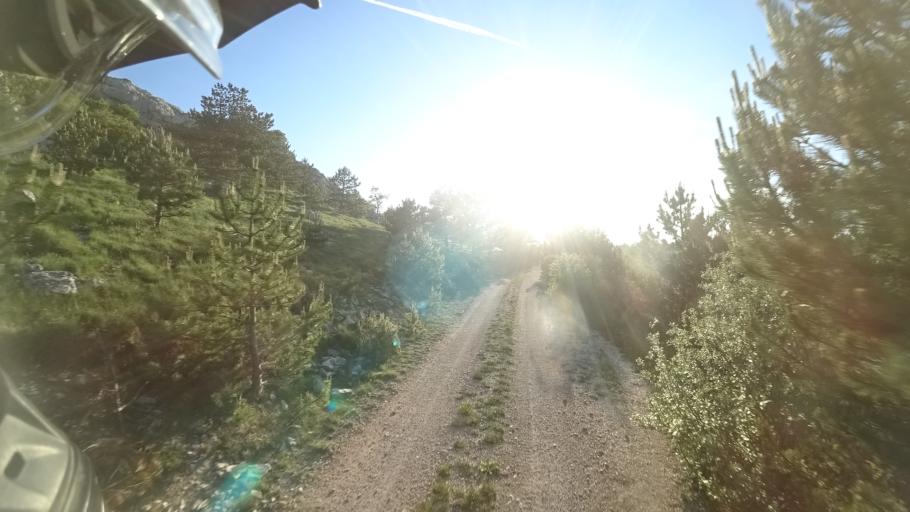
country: HR
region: Sibensko-Kniniska
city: Drnis
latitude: 43.8791
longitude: 16.3441
